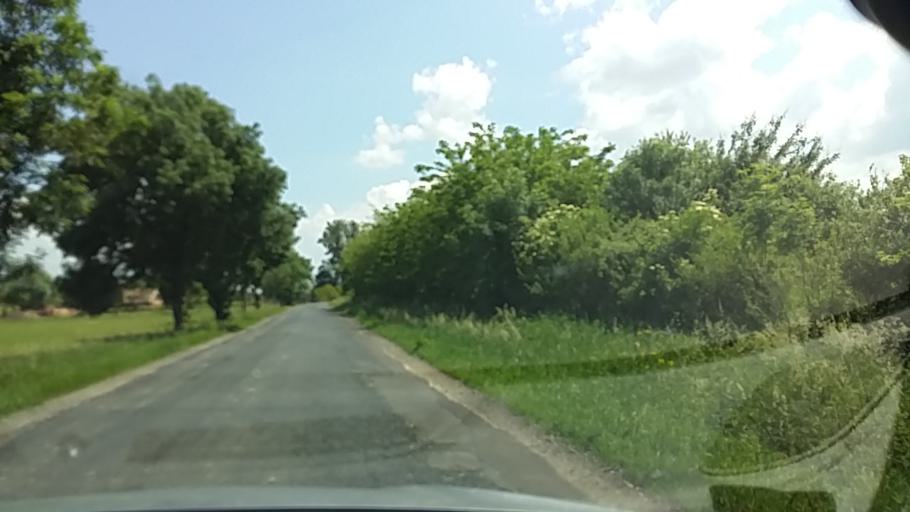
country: AT
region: Burgenland
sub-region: Politischer Bezirk Gussing
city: Moschendorf
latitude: 46.9626
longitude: 16.5146
